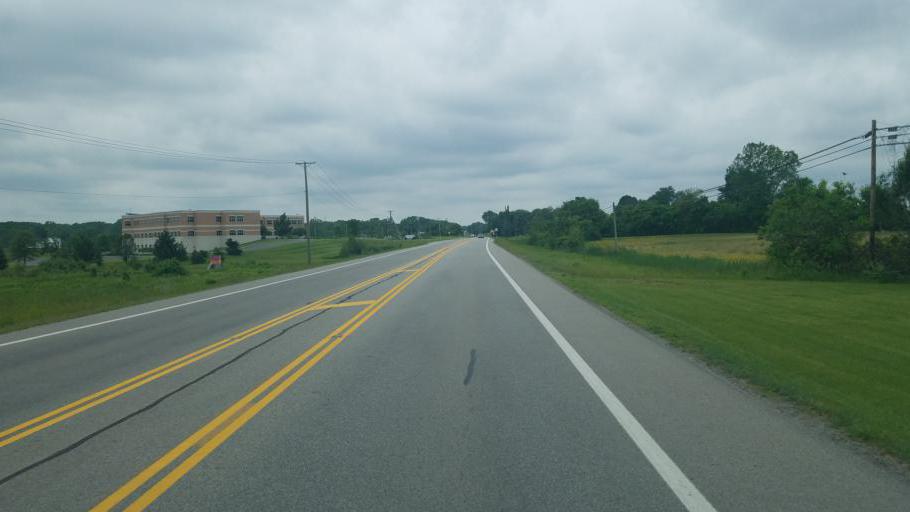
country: US
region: Ohio
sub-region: Licking County
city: Granville South
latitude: 40.0439
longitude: -82.5688
